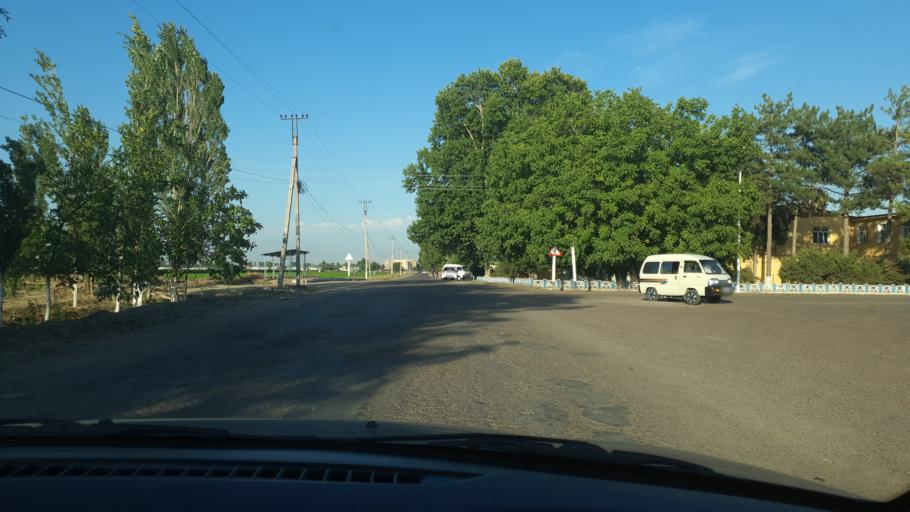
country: UZ
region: Toshkent
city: Tuytepa
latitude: 41.0857
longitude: 69.3435
